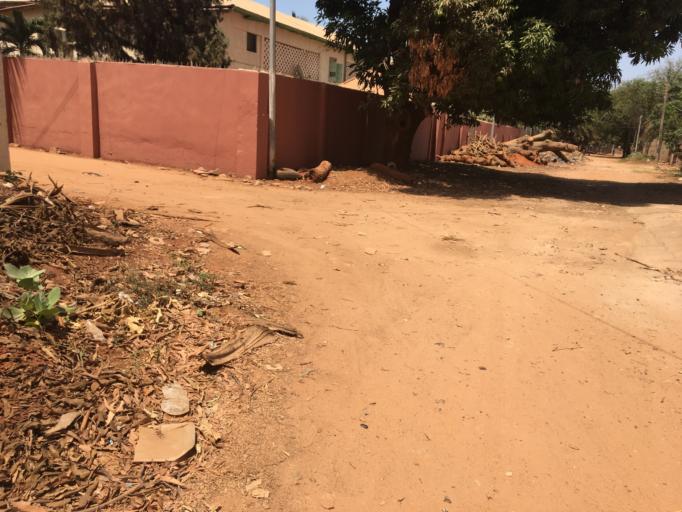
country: GM
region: Banjul
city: Bakau
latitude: 13.4760
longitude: -16.6849
